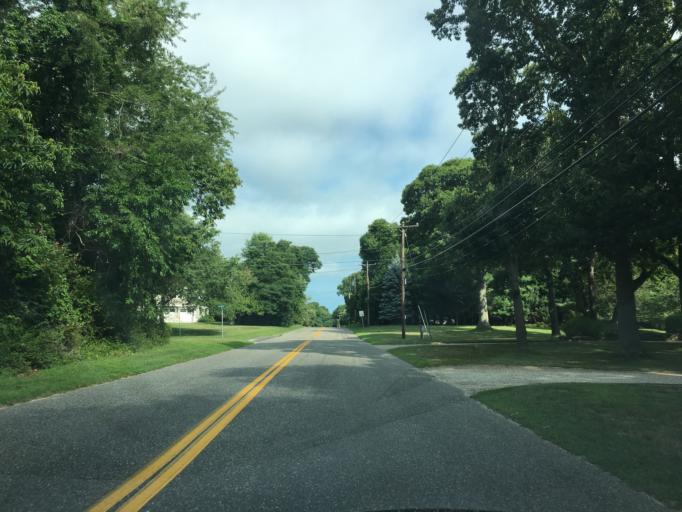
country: US
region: New York
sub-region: Suffolk County
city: Shelter Island
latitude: 41.0532
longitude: -72.3644
